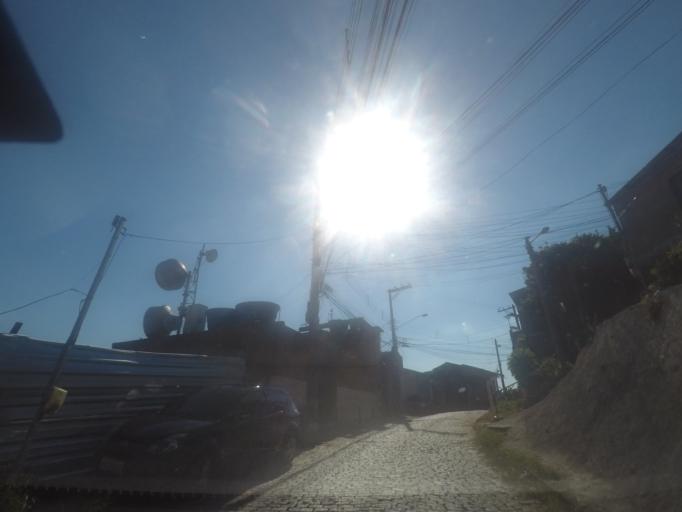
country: BR
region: Rio de Janeiro
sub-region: Petropolis
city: Petropolis
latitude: -22.5457
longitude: -43.2012
